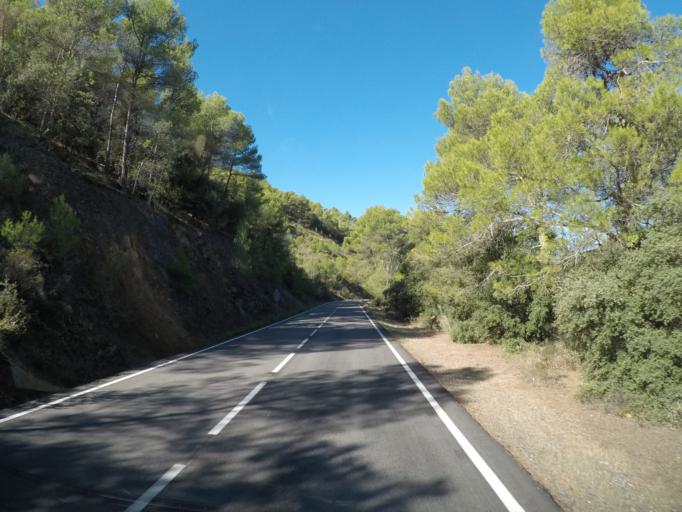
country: ES
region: Catalonia
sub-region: Provincia de Tarragona
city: Falset
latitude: 41.1671
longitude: 0.8155
